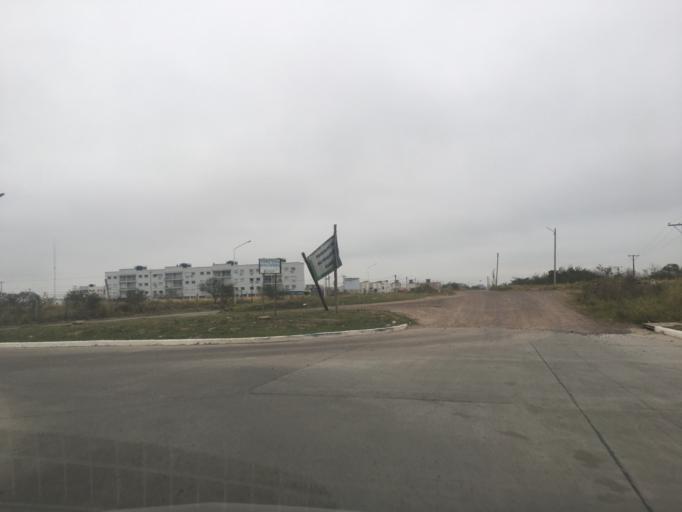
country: AR
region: Corrientes
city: Corrientes
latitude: -27.5227
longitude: -58.8006
